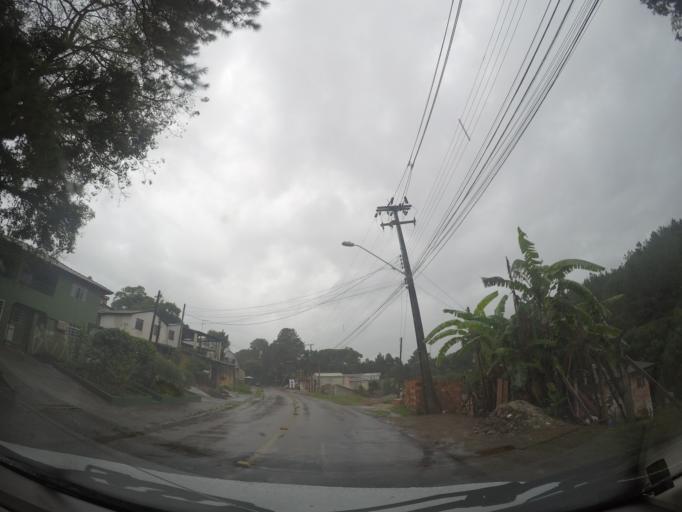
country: BR
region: Parana
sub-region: Curitiba
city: Curitiba
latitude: -25.4542
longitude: -49.3740
